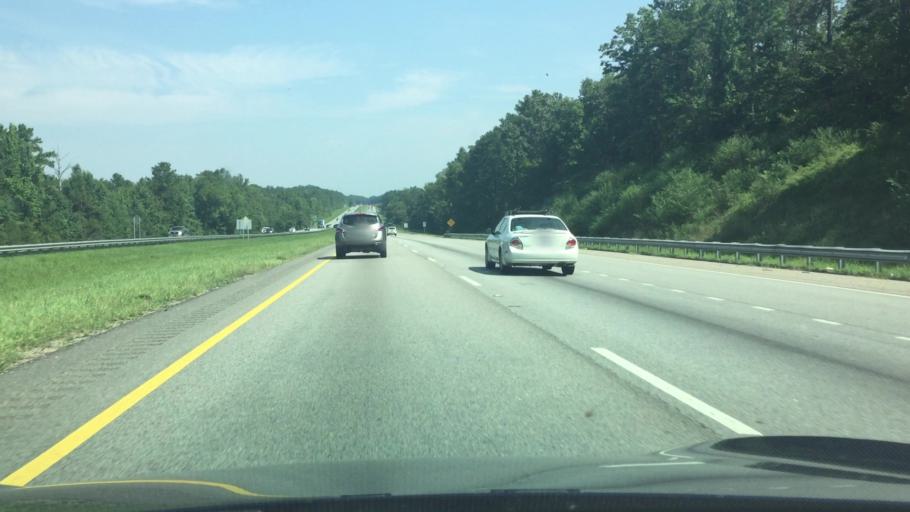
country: US
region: Alabama
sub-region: Shelby County
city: Calera
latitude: 33.1083
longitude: -86.7397
